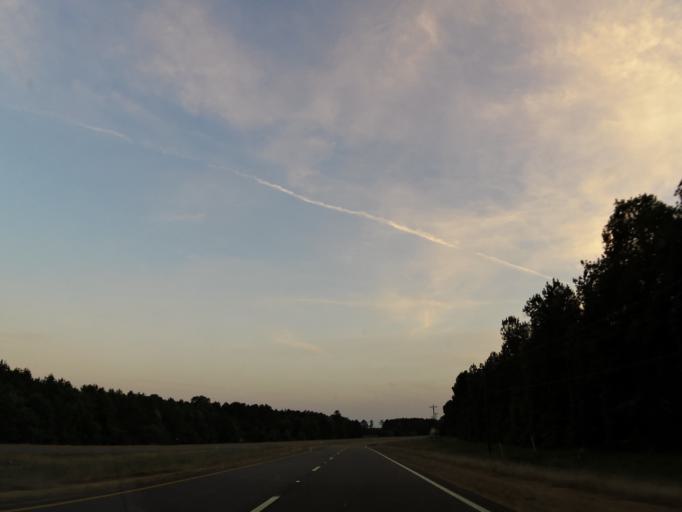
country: US
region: Mississippi
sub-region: Kemper County
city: De Kalb
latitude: 32.7386
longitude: -88.4671
